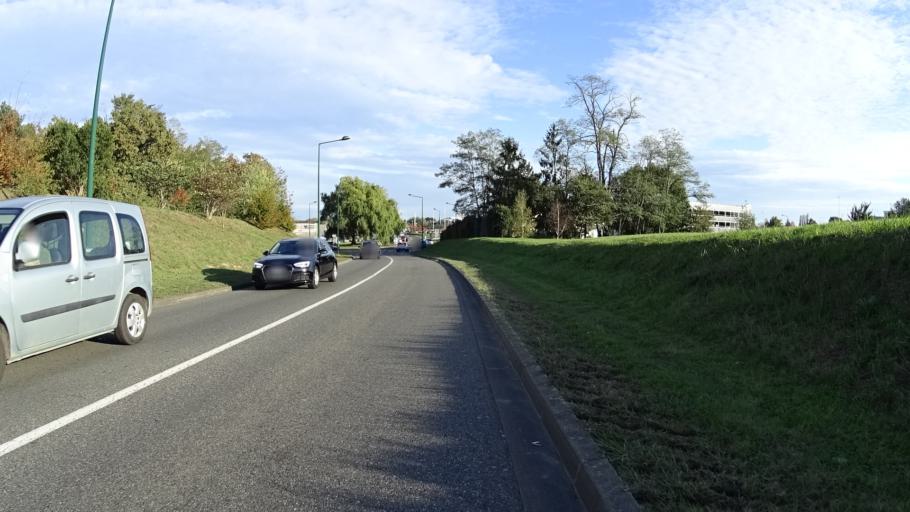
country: FR
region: Aquitaine
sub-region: Departement des Landes
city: Saint-Paul-les-Dax
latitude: 43.7333
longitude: -1.0459
